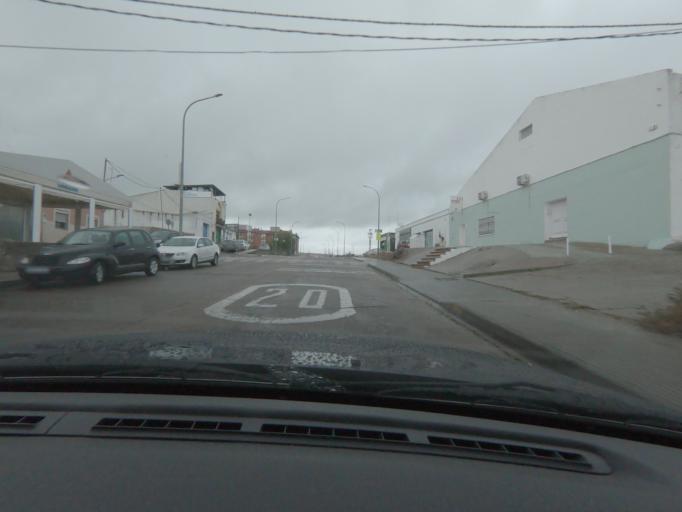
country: ES
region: Extremadura
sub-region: Provincia de Badajoz
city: Merida
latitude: 38.9269
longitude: -6.3376
